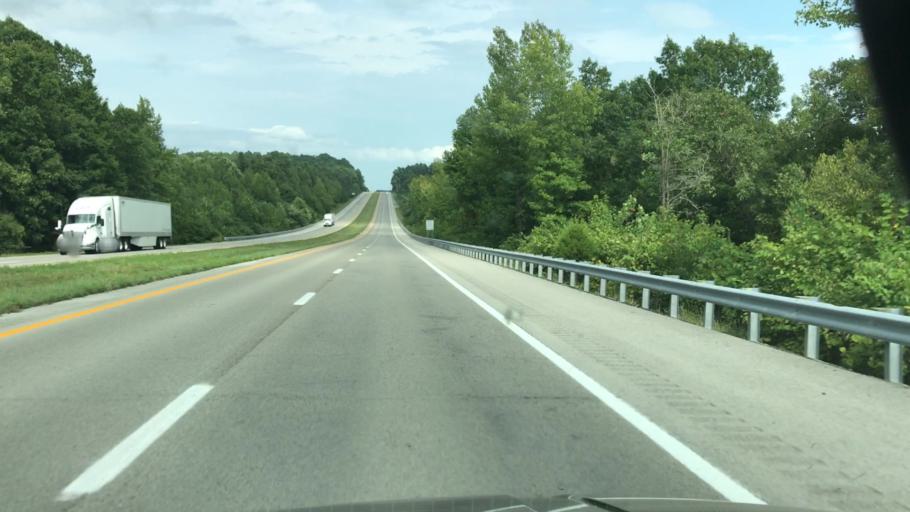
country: US
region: Kentucky
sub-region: Hopkins County
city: Earlington
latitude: 37.1993
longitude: -87.5464
